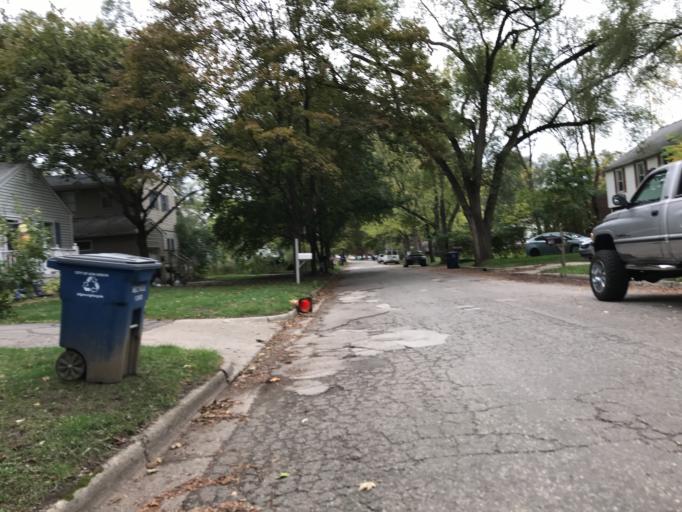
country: US
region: Michigan
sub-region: Washtenaw County
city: Ann Arbor
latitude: 42.2553
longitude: -83.7299
